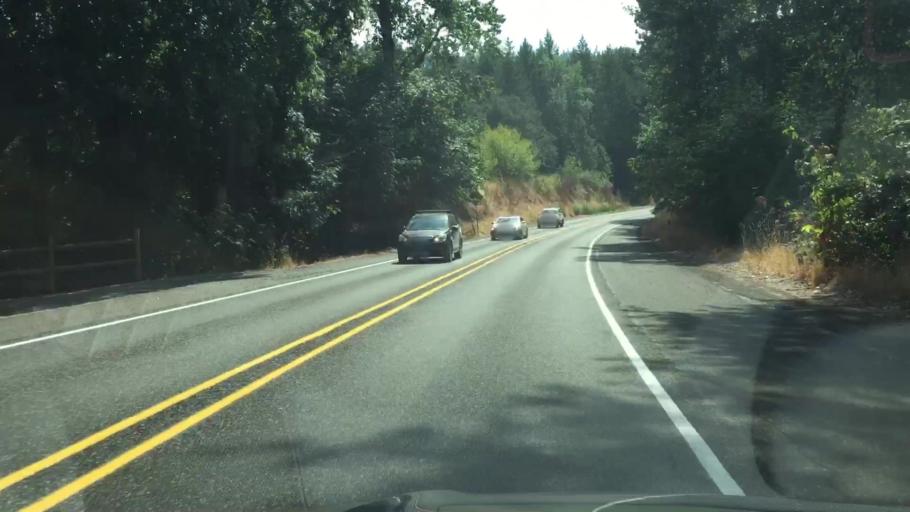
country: US
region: Washington
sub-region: Klickitat County
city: White Salmon
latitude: 45.7963
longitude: -121.4854
